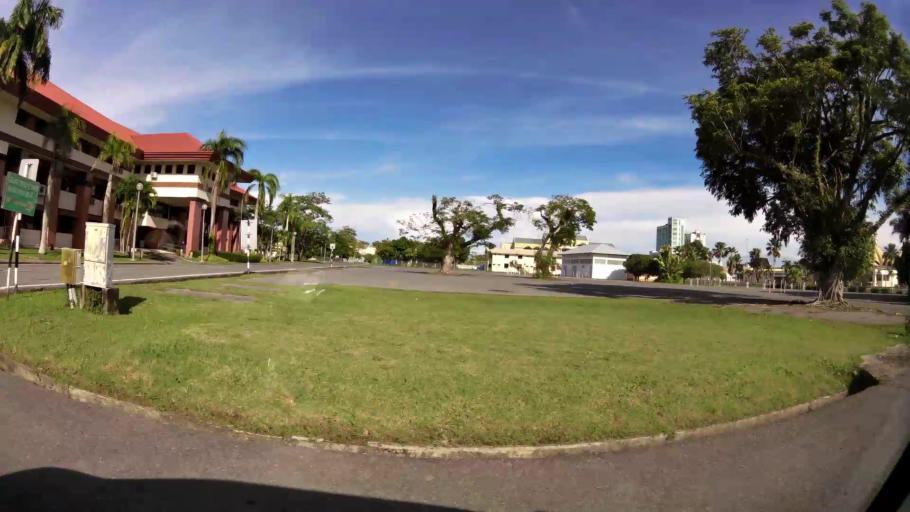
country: BN
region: Belait
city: Kuala Belait
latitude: 4.5864
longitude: 114.1906
